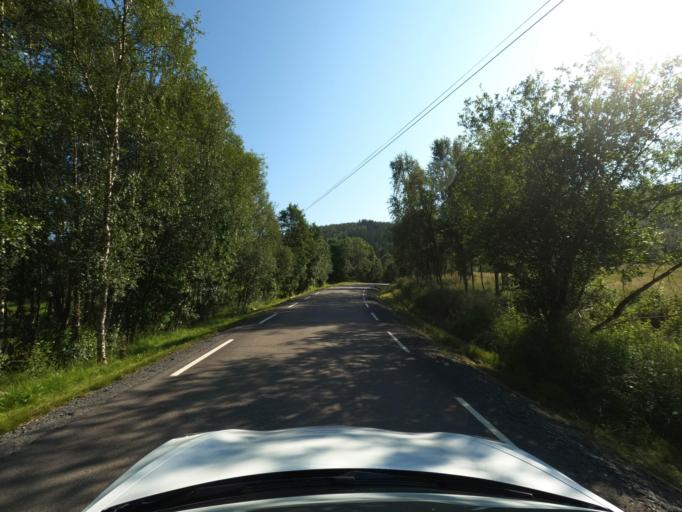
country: NO
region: Nordland
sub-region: Narvik
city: Narvik
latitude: 68.3959
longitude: 17.3028
